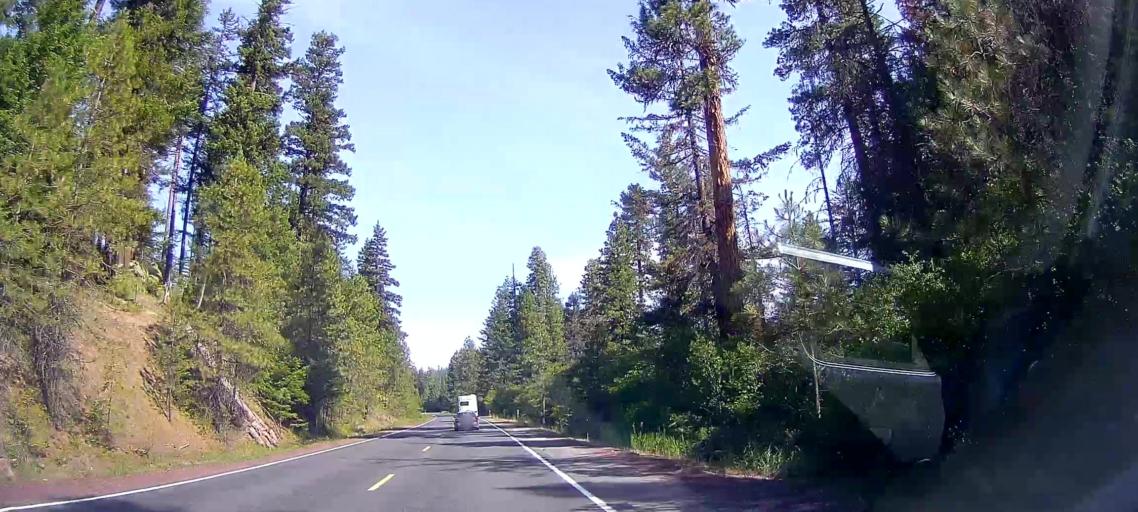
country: US
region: Oregon
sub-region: Jefferson County
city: Warm Springs
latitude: 45.0535
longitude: -121.5119
